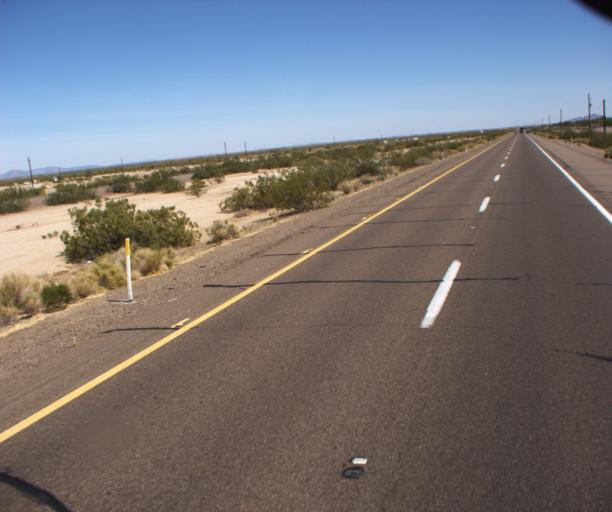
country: US
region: Arizona
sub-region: Yuma County
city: Wellton
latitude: 32.7357
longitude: -113.7005
